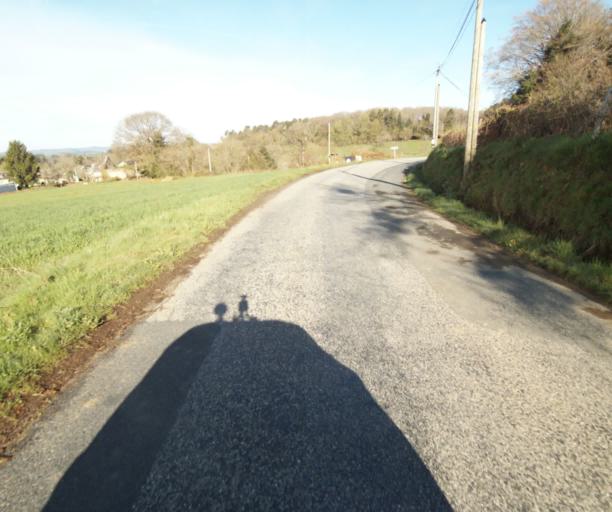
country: FR
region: Limousin
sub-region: Departement de la Correze
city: Laguenne
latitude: 45.2754
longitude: 1.8583
